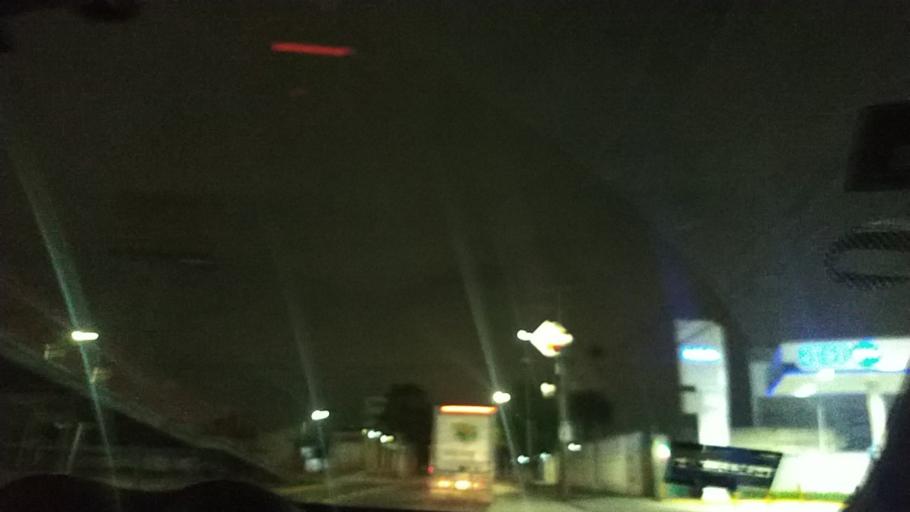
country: MX
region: Mexico
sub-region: Tultitlan
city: Colonia Lazaro Cardenas (Los Hornos)
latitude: 19.6263
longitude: -99.1469
